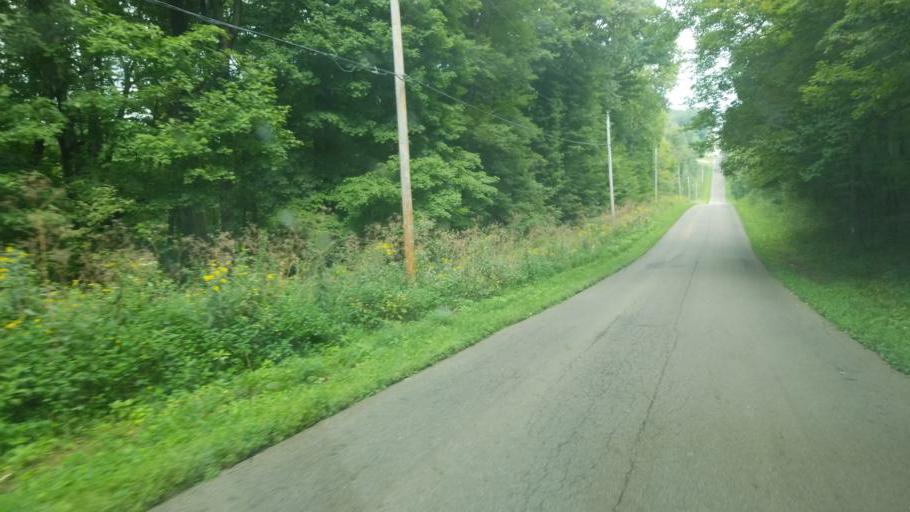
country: US
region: Ohio
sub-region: Knox County
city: Danville
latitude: 40.4565
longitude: -82.3271
